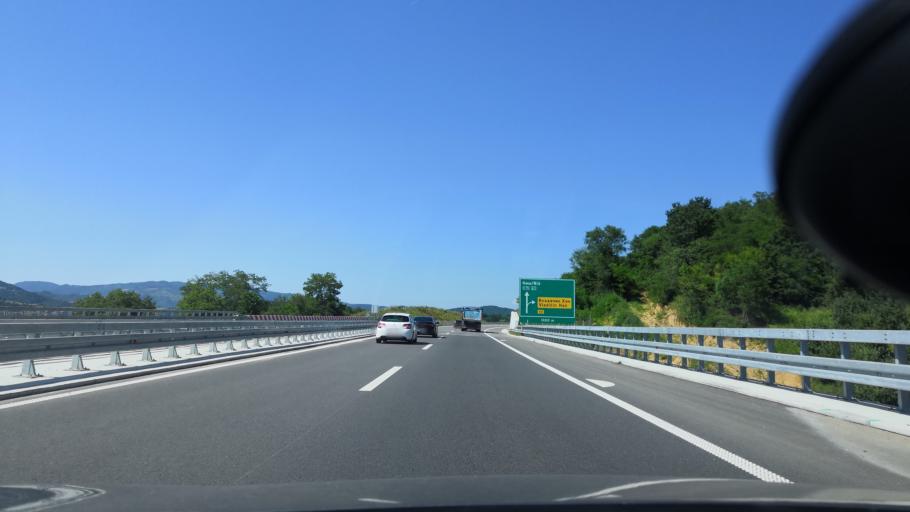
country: RS
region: Central Serbia
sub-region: Pcinjski Okrug
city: Vladicin Han
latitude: 42.6885
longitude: 22.0738
